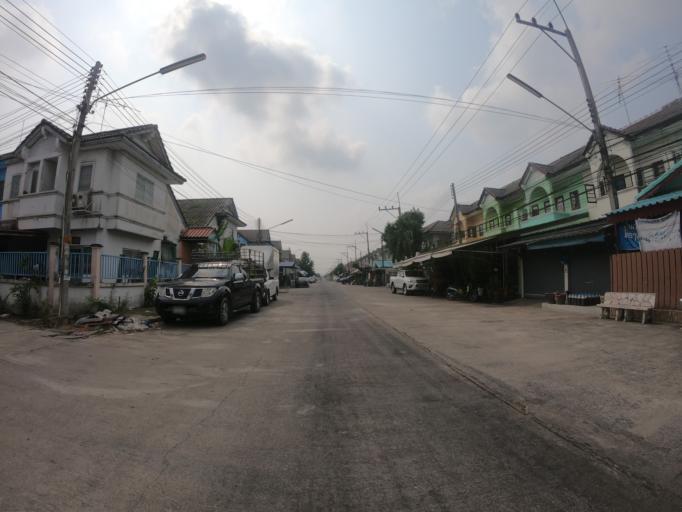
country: TH
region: Pathum Thani
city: Nong Suea
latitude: 14.0743
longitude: 100.8585
